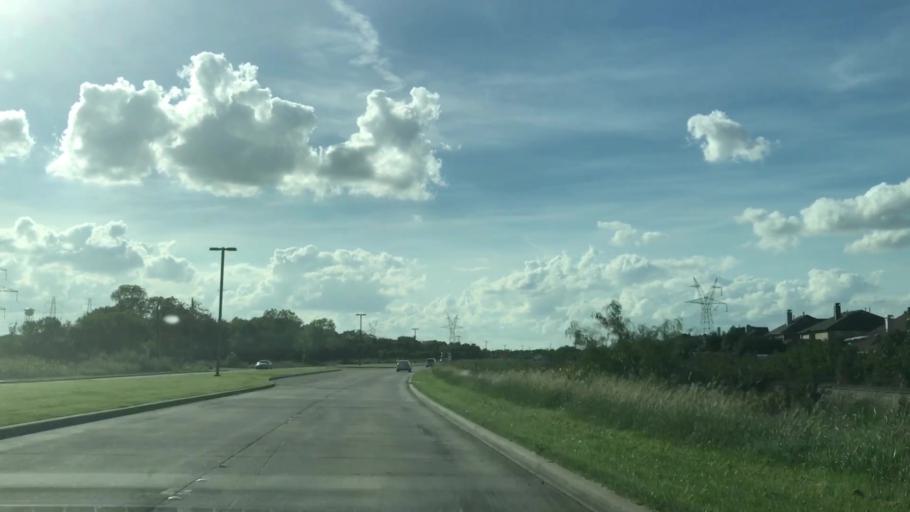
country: US
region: Texas
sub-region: Dallas County
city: Coppell
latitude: 32.9532
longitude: -96.9626
